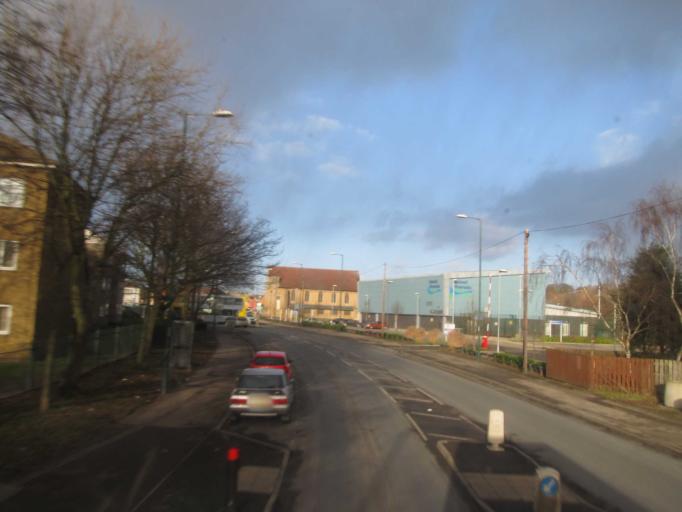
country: GB
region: England
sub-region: Nottinghamshire
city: Hucknall
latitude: 52.9959
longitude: -1.1973
